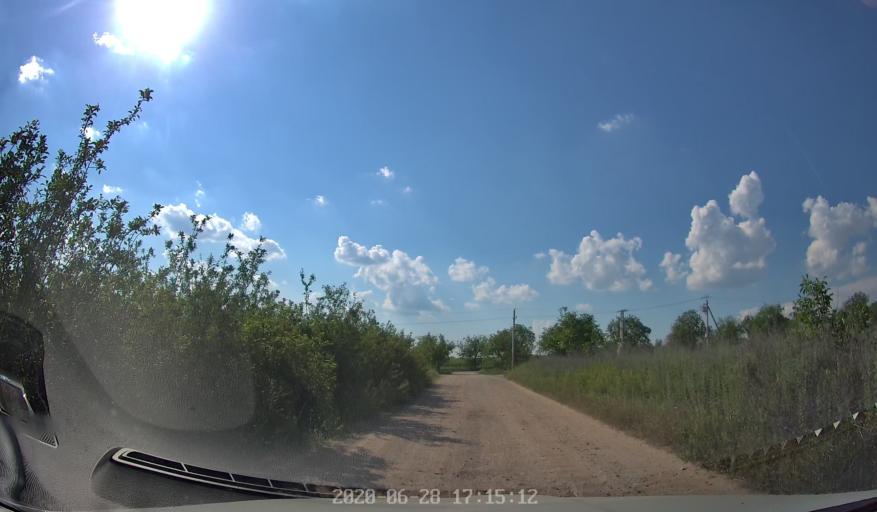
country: MD
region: Chisinau
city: Vatra
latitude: 46.9940
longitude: 28.6939
